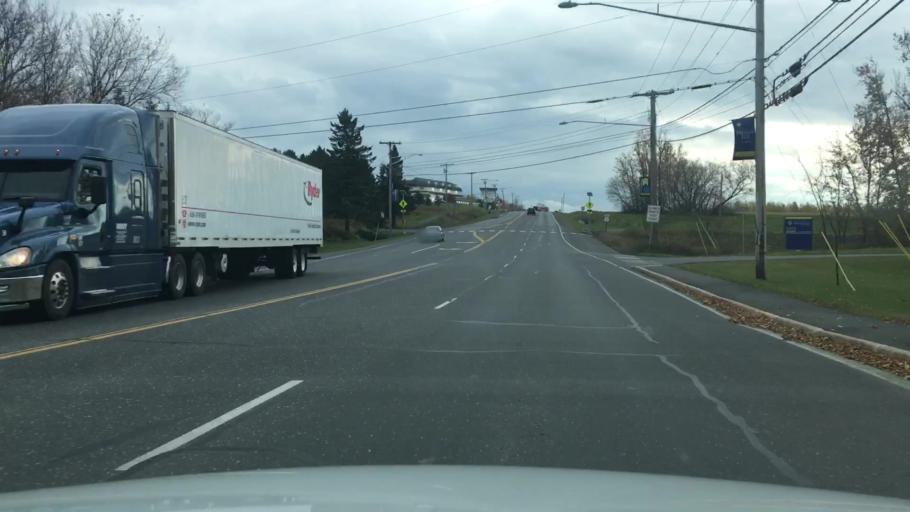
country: US
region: Maine
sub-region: Aroostook County
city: Presque Isle
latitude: 46.6707
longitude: -68.0140
